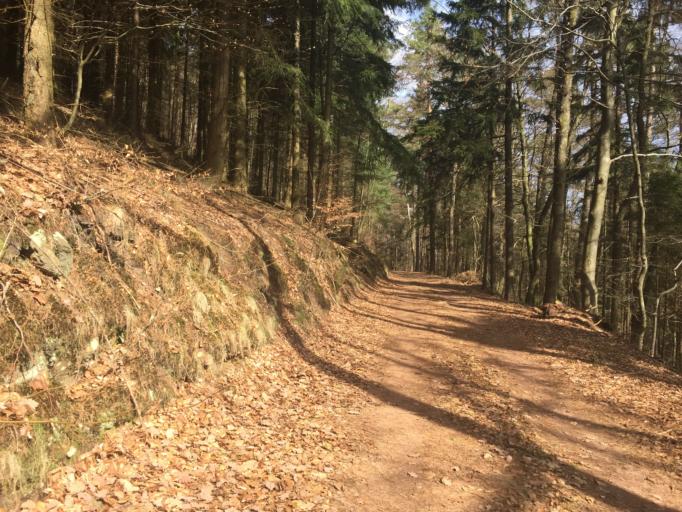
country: DE
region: Rheinland-Pfalz
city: Ramberg
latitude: 49.3062
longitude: 8.0219
